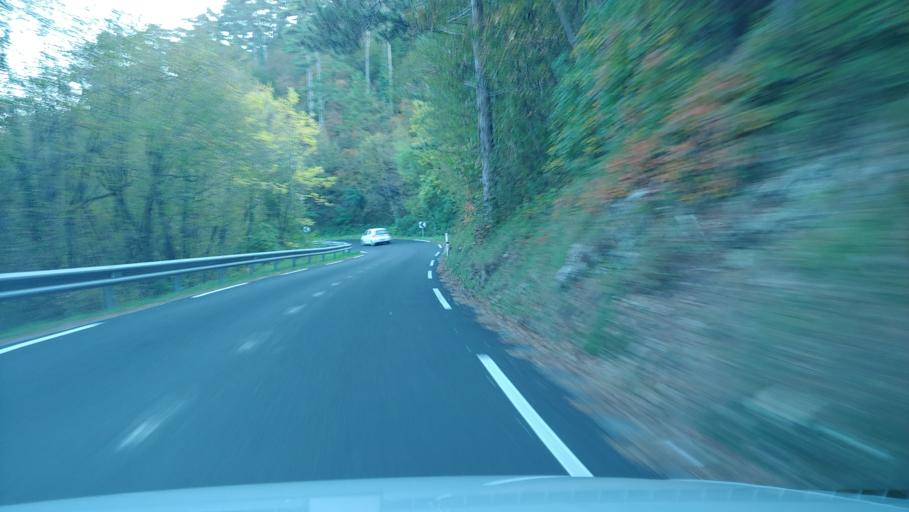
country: SI
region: Ajdovscina
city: Ajdovscina
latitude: 45.8098
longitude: 13.8571
